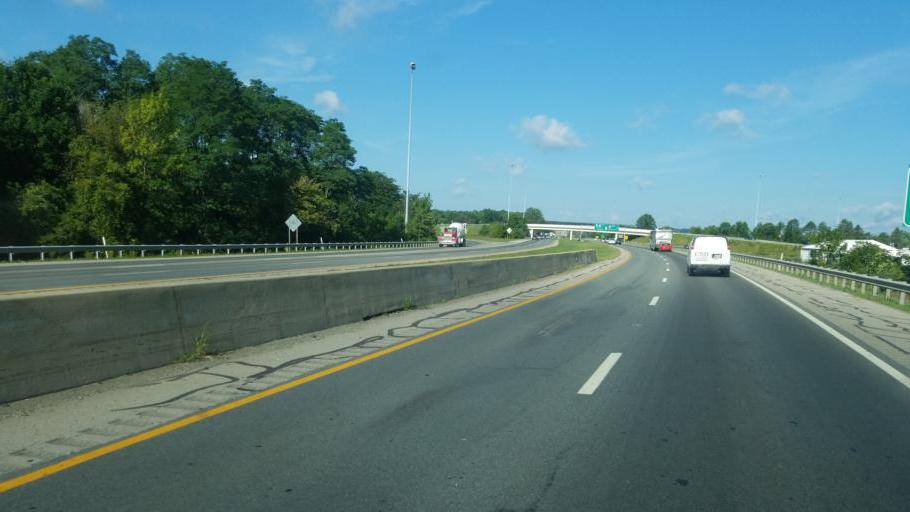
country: US
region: Ohio
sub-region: Wayne County
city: Wooster
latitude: 40.7933
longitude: -81.9462
